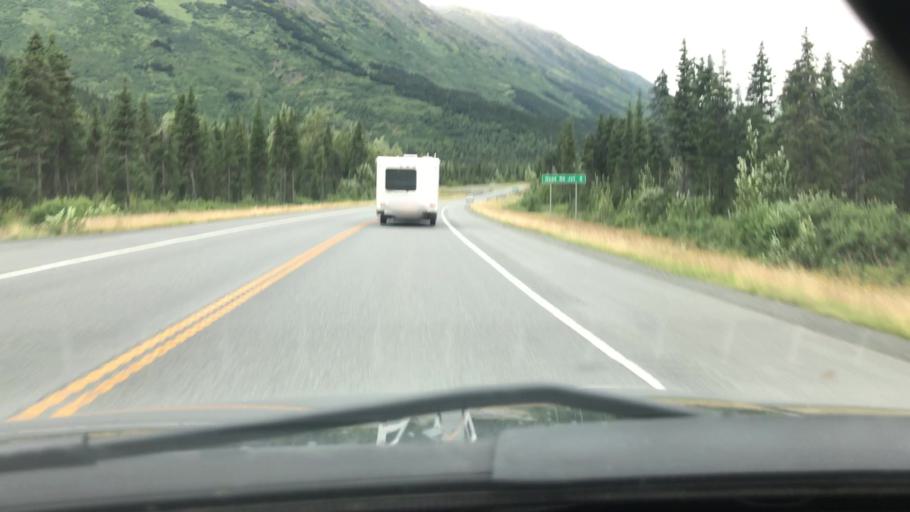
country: US
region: Alaska
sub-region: Anchorage Municipality
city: Girdwood
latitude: 60.7305
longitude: -149.3327
